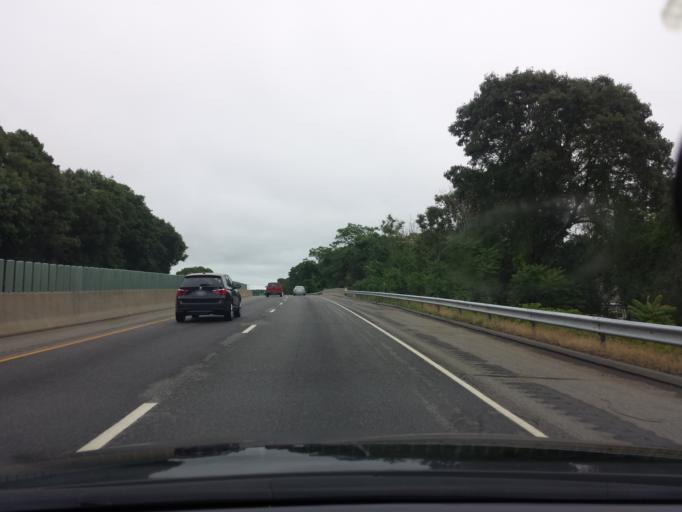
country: US
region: Connecticut
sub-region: Middlesex County
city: Old Saybrook Center
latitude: 41.3097
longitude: -72.3681
